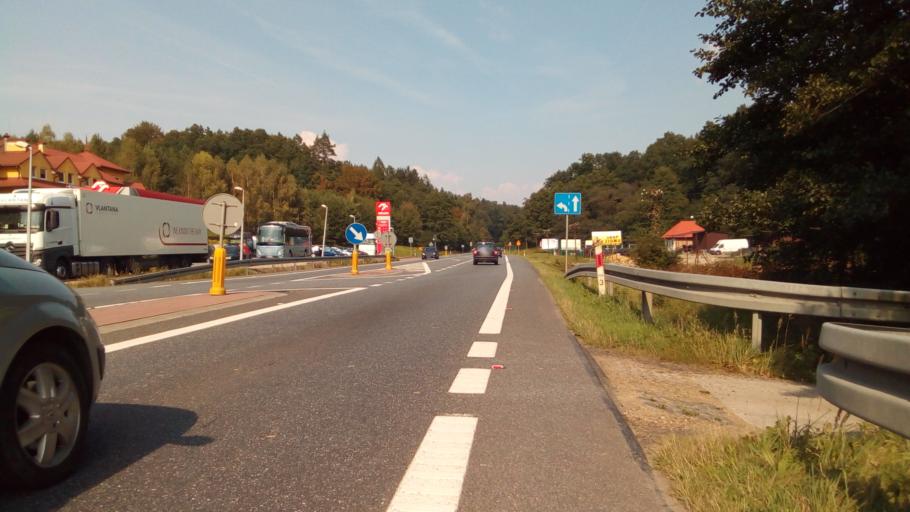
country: PL
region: Subcarpathian Voivodeship
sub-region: Powiat strzyzowski
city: Jawornik
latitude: 49.8247
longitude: 21.8751
